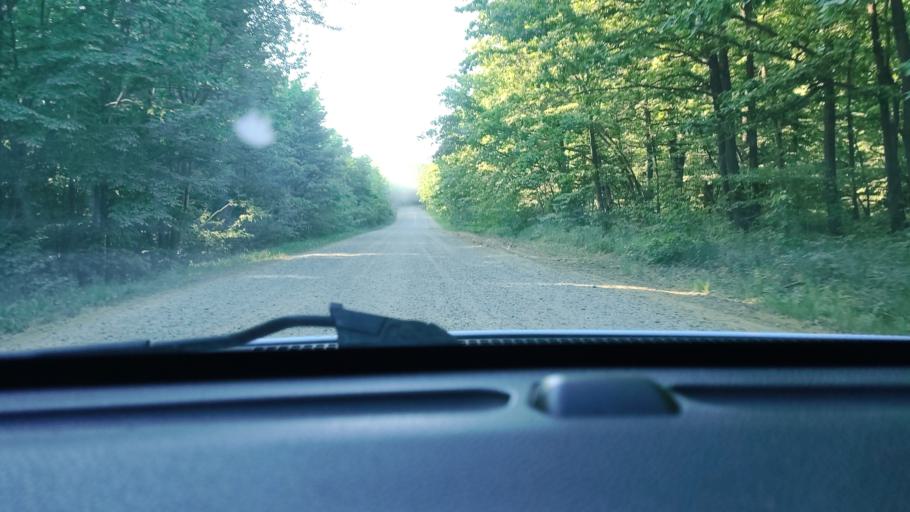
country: RU
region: Krasnodarskiy
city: Goryachiy Klyuch
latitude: 44.7105
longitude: 38.9922
